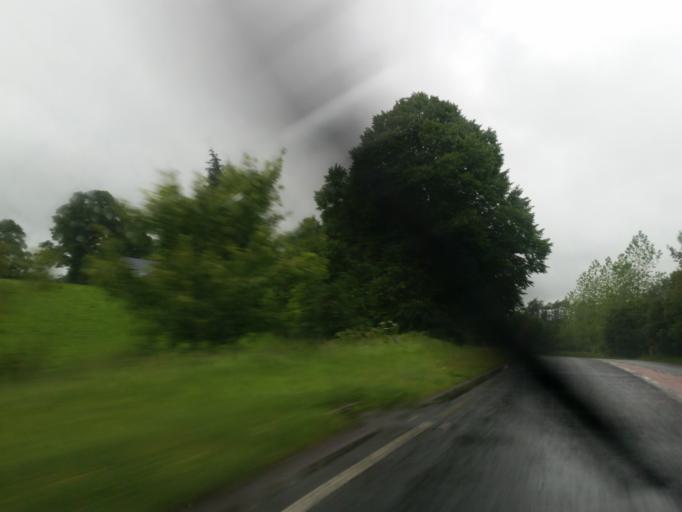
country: GB
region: Northern Ireland
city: Fivemiletown
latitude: 54.3820
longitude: -7.2842
